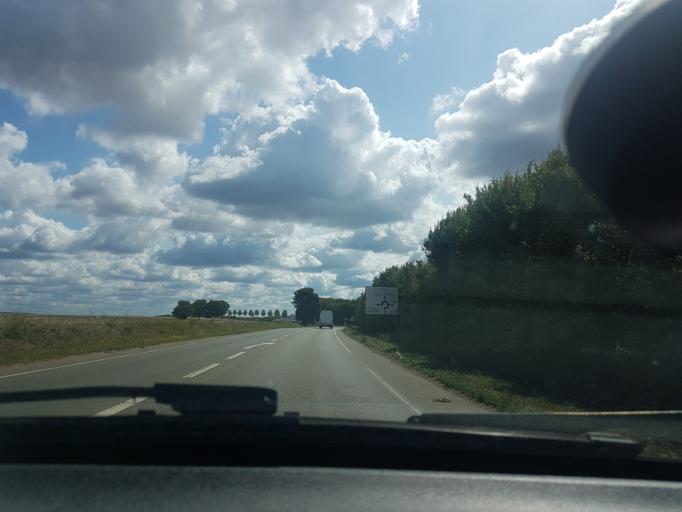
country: FR
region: Ile-de-France
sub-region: Departement des Yvelines
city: Plaisir
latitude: 48.8356
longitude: 1.9546
